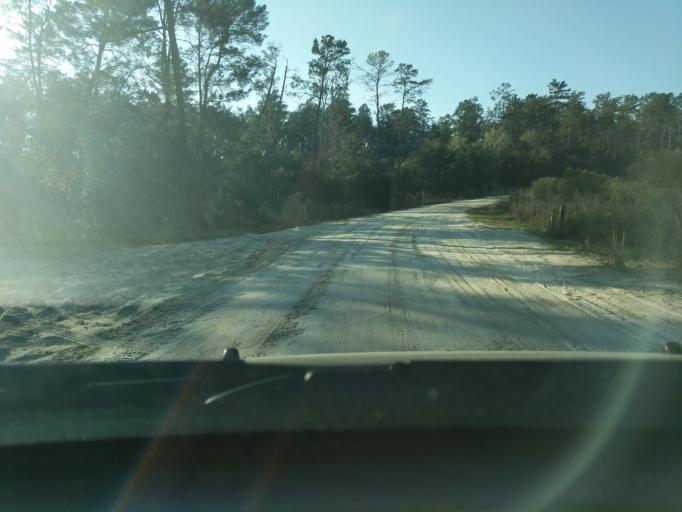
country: US
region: Florida
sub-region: Marion County
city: Silver Springs Shores
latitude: 29.2161
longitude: -81.8235
